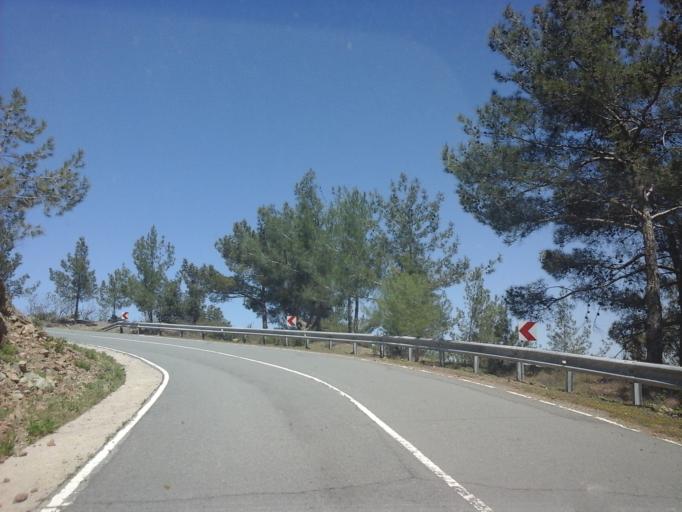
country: CY
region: Lefkosia
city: Kakopetria
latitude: 35.0028
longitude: 32.7914
